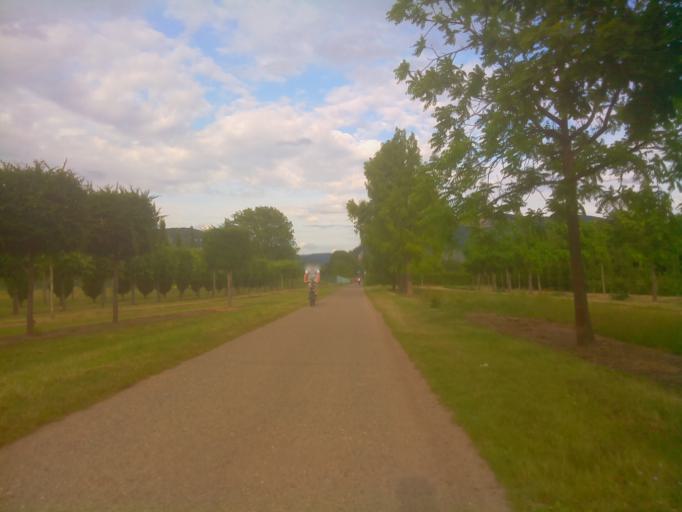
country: DE
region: Baden-Wuerttemberg
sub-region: Karlsruhe Region
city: Ladenburg
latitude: 49.4761
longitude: 8.6336
